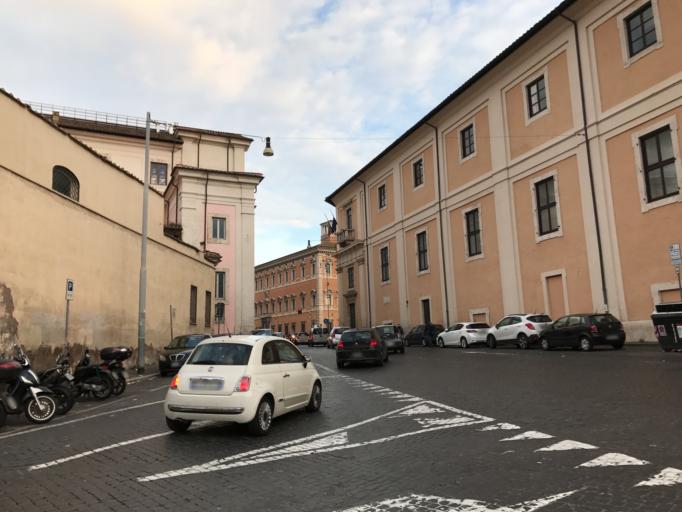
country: IT
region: Latium
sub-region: Citta metropolitana di Roma Capitale
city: Rome
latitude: 41.8873
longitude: 12.5031
